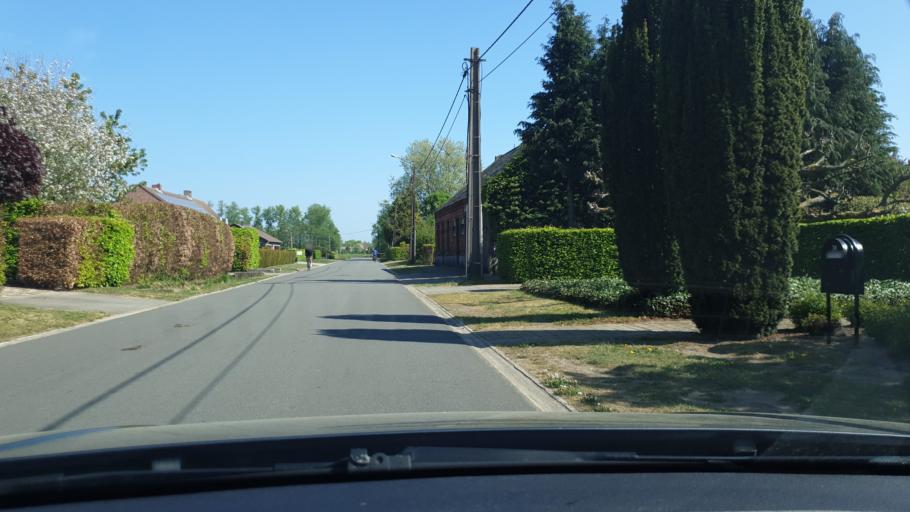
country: BE
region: Flanders
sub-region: Provincie Antwerpen
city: Geel
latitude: 51.1408
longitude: 4.9912
